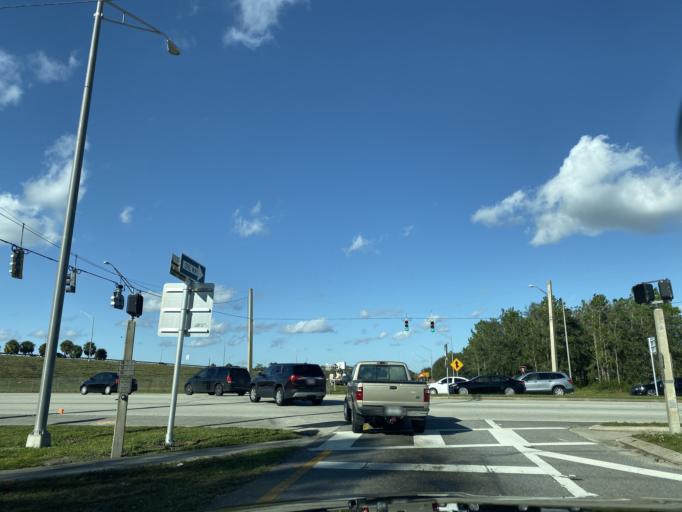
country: US
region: Florida
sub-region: Orange County
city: Union Park
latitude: 28.5681
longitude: -81.2647
